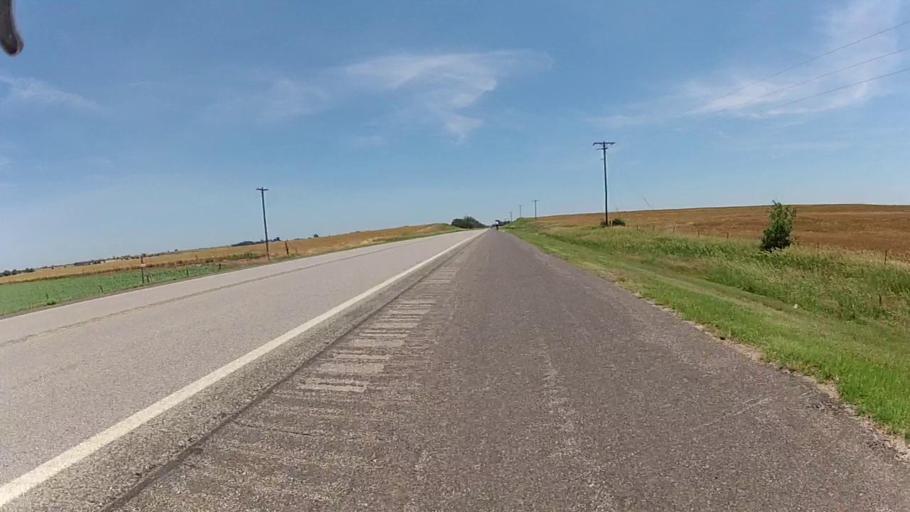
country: US
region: Kansas
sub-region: Barber County
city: Medicine Lodge
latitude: 37.2536
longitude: -98.3907
